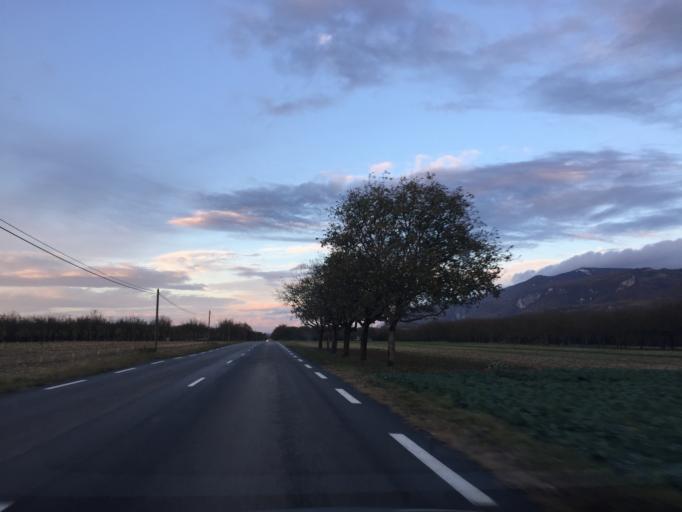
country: FR
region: Rhone-Alpes
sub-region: Departement de l'Isere
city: Saint-Just-de-Claix
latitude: 45.0956
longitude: 5.3045
